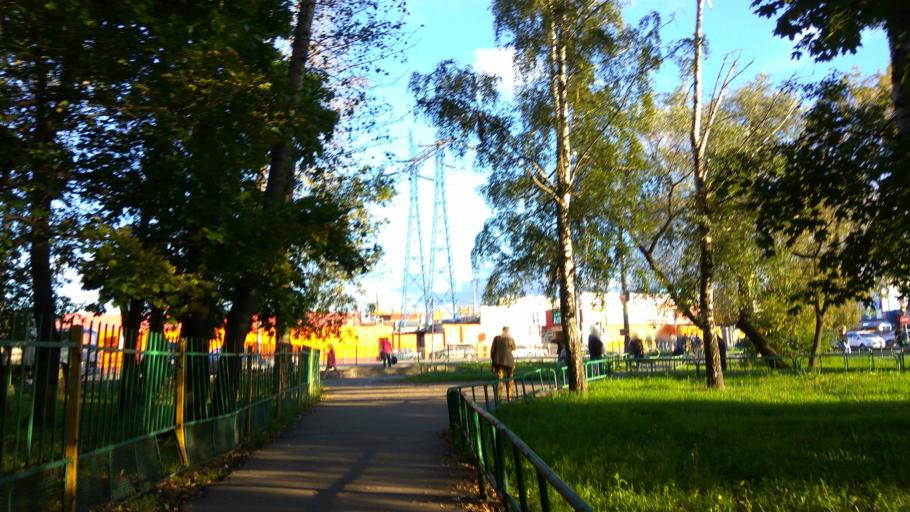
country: RU
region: Moscow
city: Likhobory
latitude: 55.8380
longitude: 37.5741
